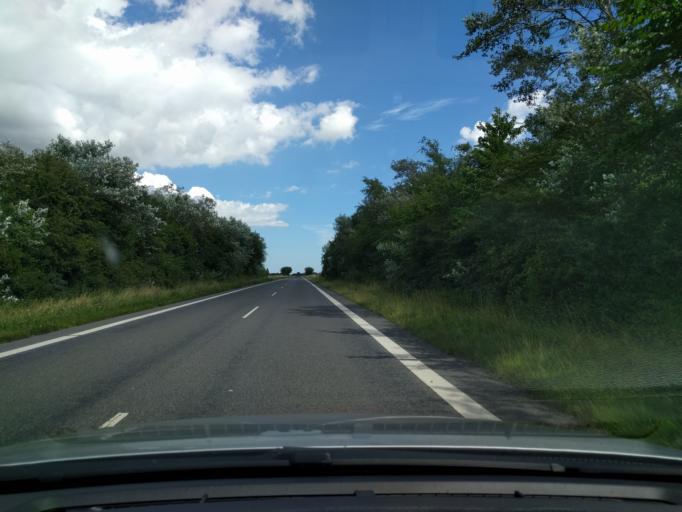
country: DK
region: Zealand
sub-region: Guldborgsund Kommune
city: Stubbekobing
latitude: 54.9241
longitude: 12.1672
